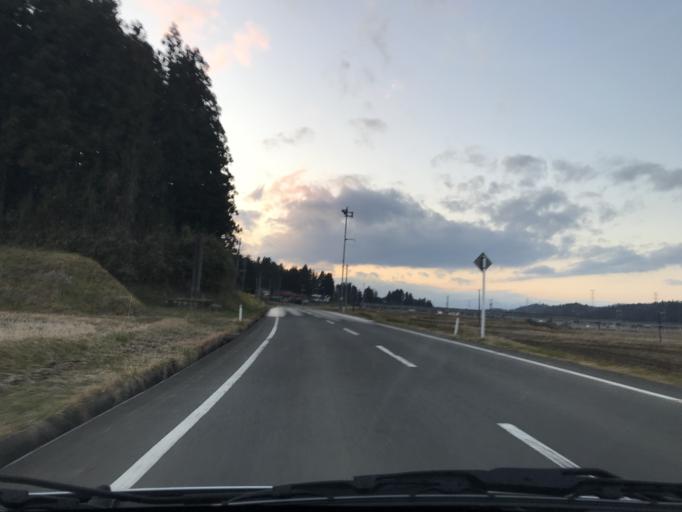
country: JP
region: Iwate
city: Ichinoseki
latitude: 38.8440
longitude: 141.1164
